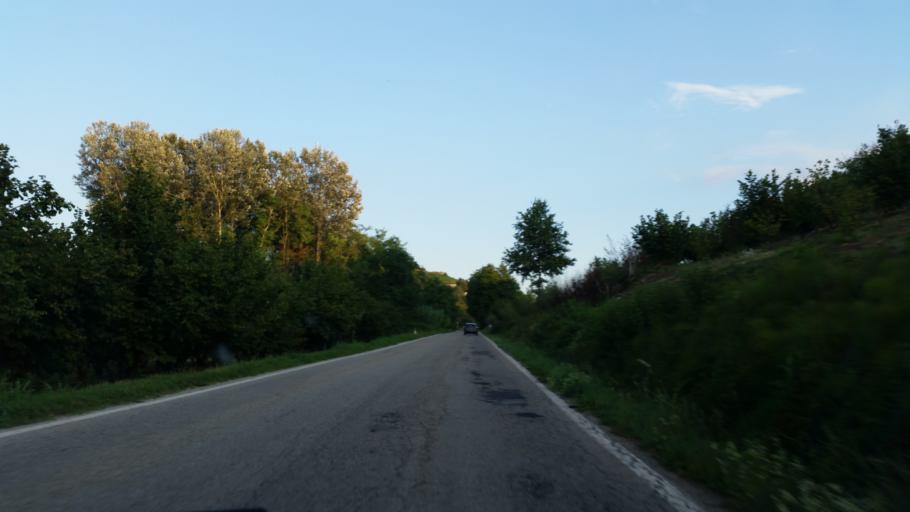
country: IT
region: Piedmont
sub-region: Provincia di Cuneo
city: Neive-Borgonovo
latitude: 44.7156
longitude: 8.1238
